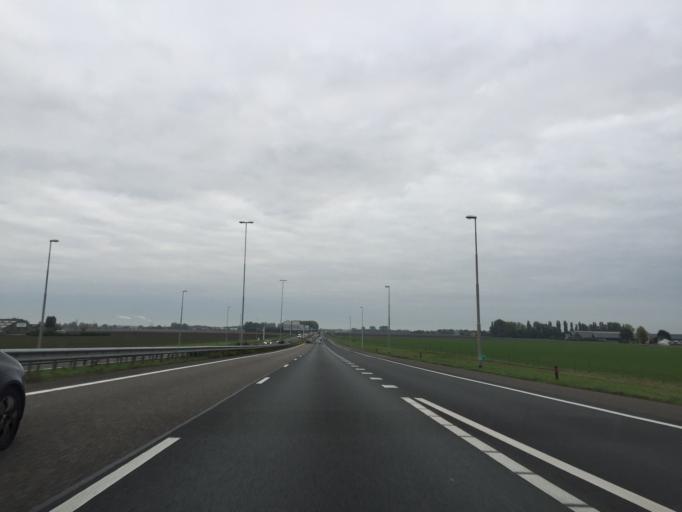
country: NL
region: North Brabant
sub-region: Gemeente Breda
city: Breda
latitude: 51.6464
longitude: 4.6972
